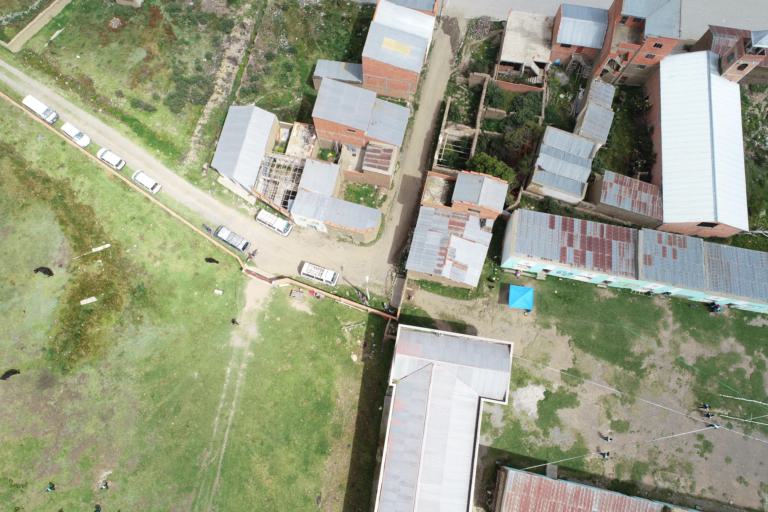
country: BO
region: La Paz
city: Achacachi
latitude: -16.0210
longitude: -68.6182
